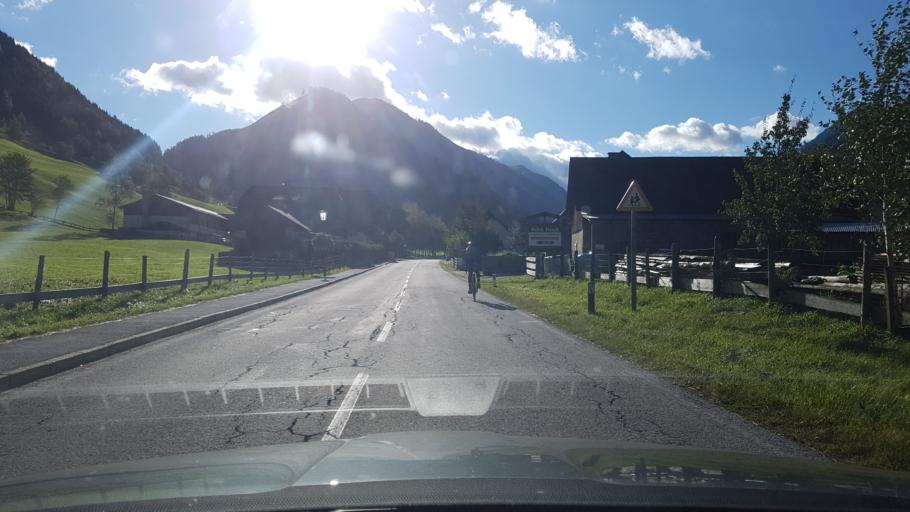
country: AT
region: Styria
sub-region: Politischer Bezirk Liezen
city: Sankt Nikolai im Solktal
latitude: 47.3496
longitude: 14.0254
